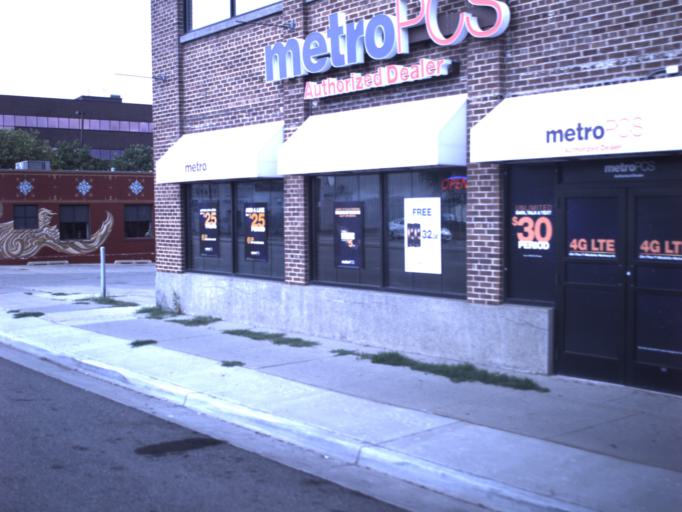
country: US
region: Utah
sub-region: Salt Lake County
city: South Salt Lake
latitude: 40.7385
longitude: -111.8881
